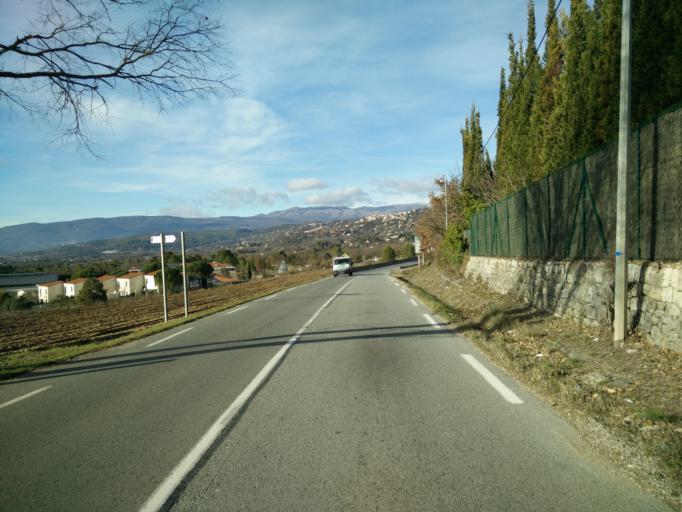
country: FR
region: Provence-Alpes-Cote d'Azur
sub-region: Departement du Var
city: Montauroux
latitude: 43.5970
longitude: 6.7871
